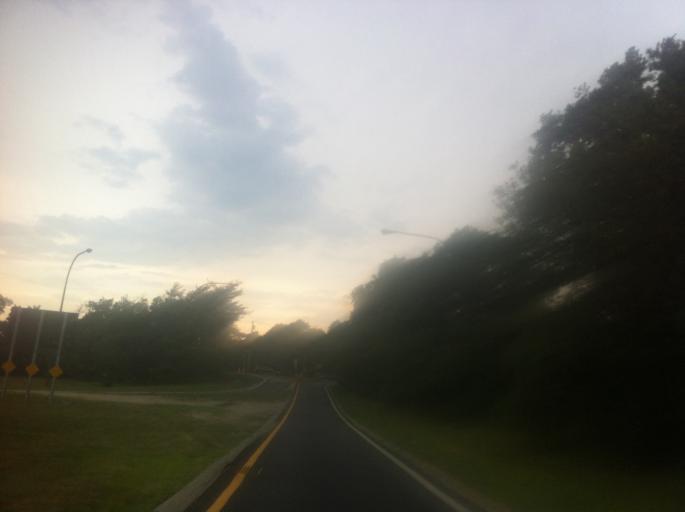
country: US
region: New York
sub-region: Nassau County
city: Jericho
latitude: 40.7896
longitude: -73.5199
